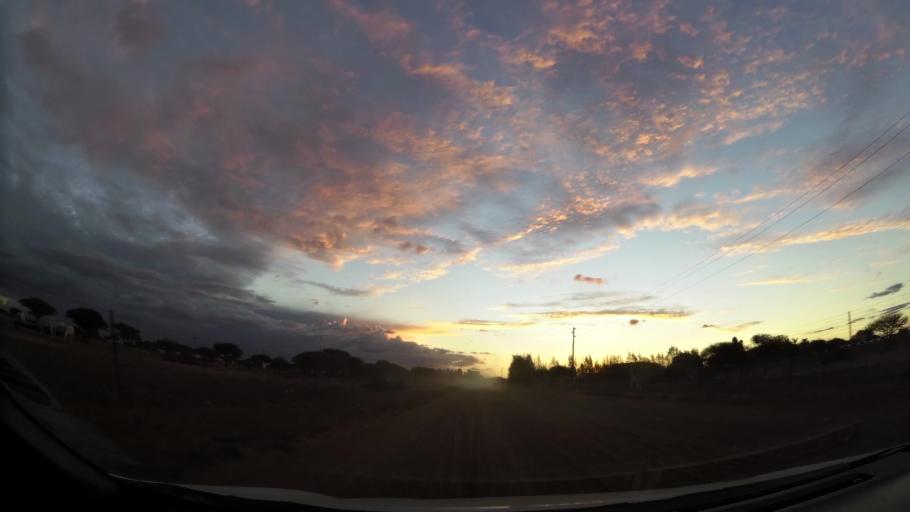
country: ZA
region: Limpopo
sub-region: Capricorn District Municipality
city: Polokwane
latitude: -23.7351
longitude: 29.4263
